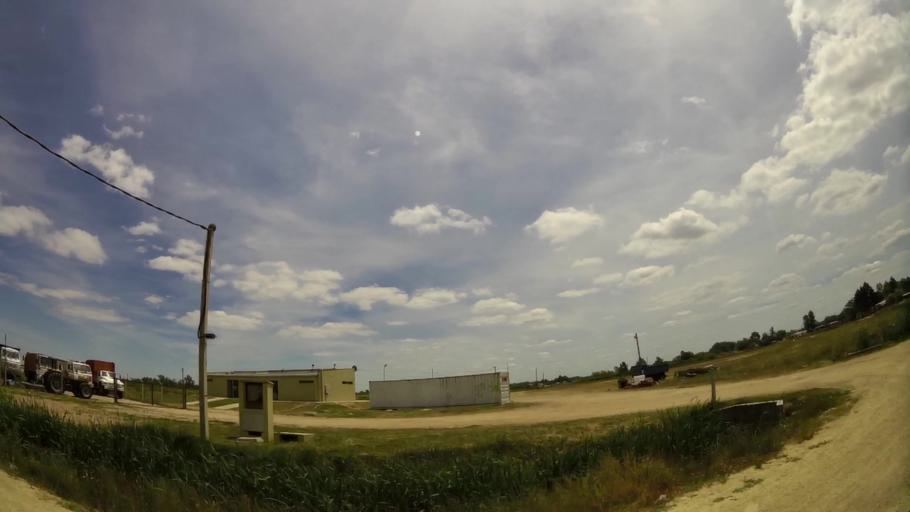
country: UY
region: San Jose
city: Delta del Tigre
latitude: -34.7616
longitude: -56.4111
